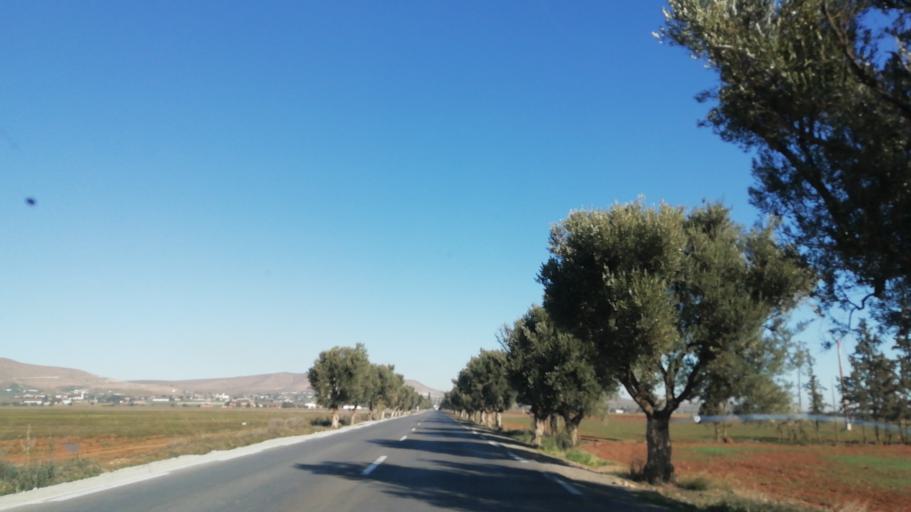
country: DZ
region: Mascara
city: Mascara
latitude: 35.2058
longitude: 0.1098
